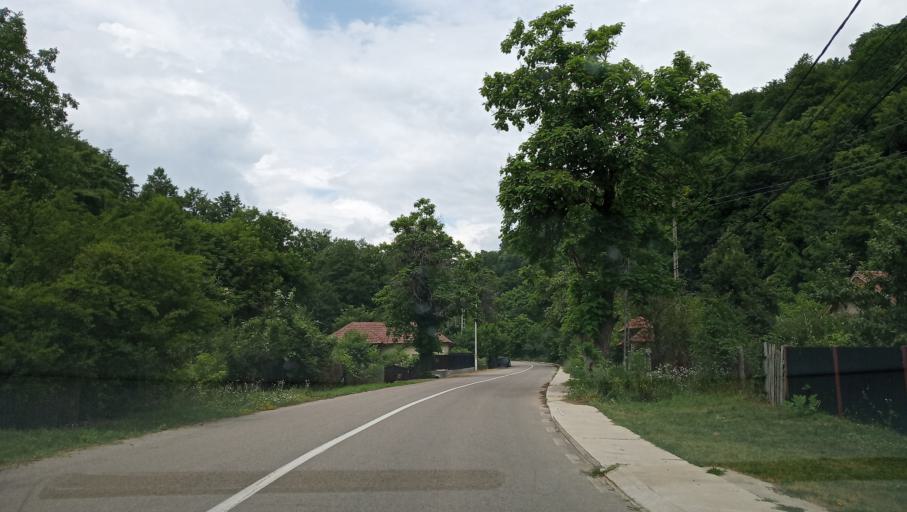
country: RO
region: Gorj
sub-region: Comuna Tismana
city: Pocruia
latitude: 45.0690
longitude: 22.9393
